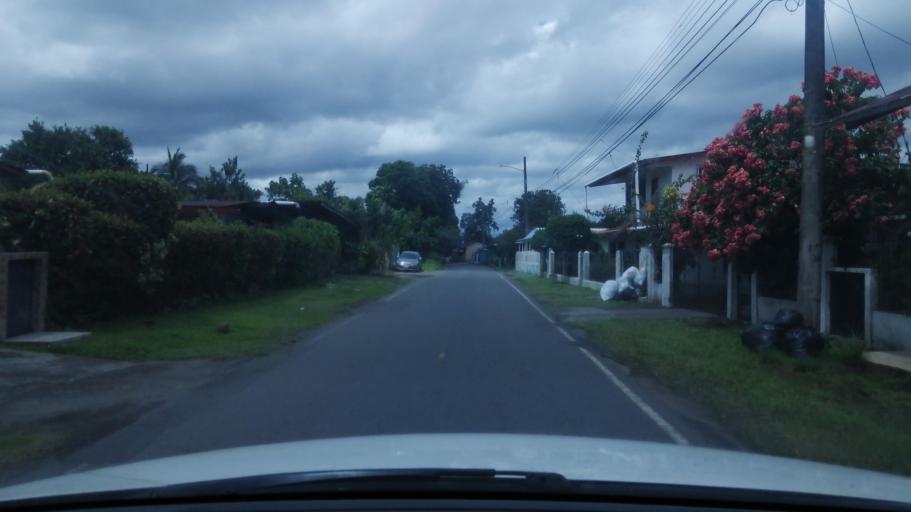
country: PA
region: Chiriqui
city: David
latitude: 8.4305
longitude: -82.4181
